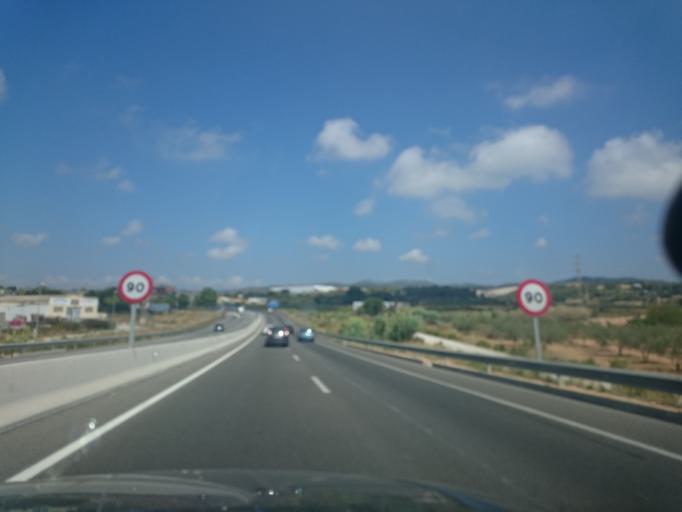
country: ES
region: Catalonia
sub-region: Provincia de Barcelona
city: Vilanova i la Geltru
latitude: 41.2395
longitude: 1.7319
